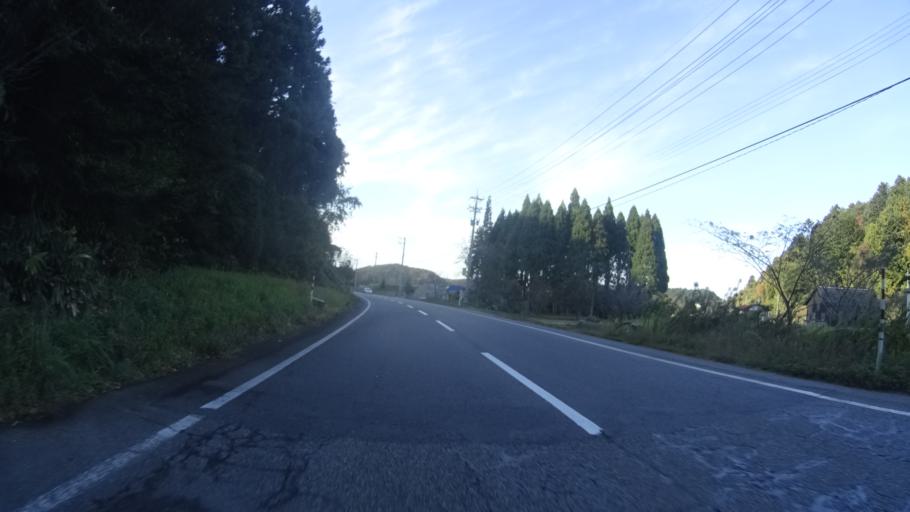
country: JP
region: Ishikawa
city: Hakui
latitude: 37.0158
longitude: 136.7953
